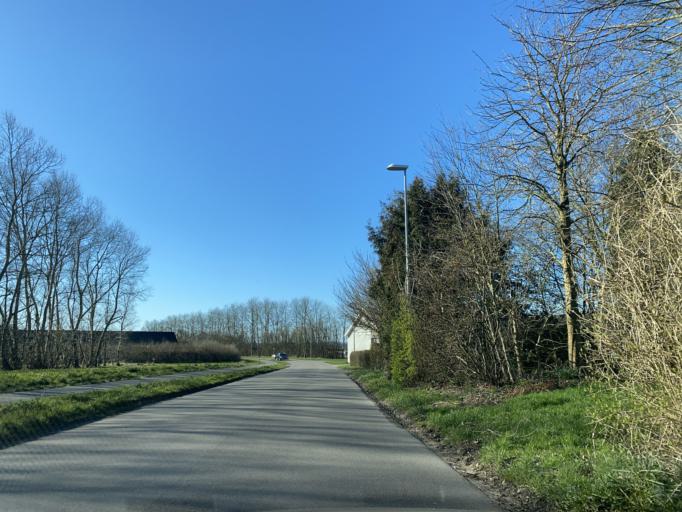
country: DK
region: Central Jutland
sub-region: Skanderborg Kommune
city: Skovby
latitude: 56.1878
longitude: 9.9631
